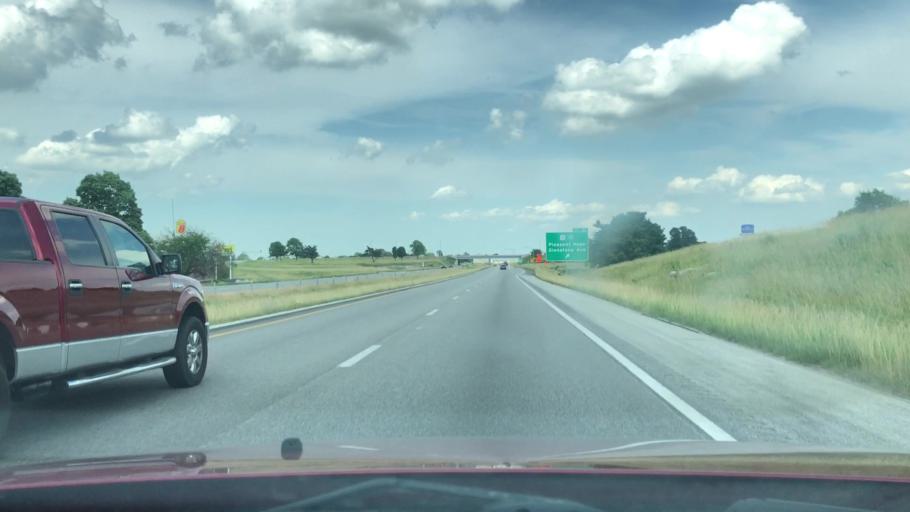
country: US
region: Missouri
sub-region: Greene County
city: Springfield
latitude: 37.2501
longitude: -93.2698
